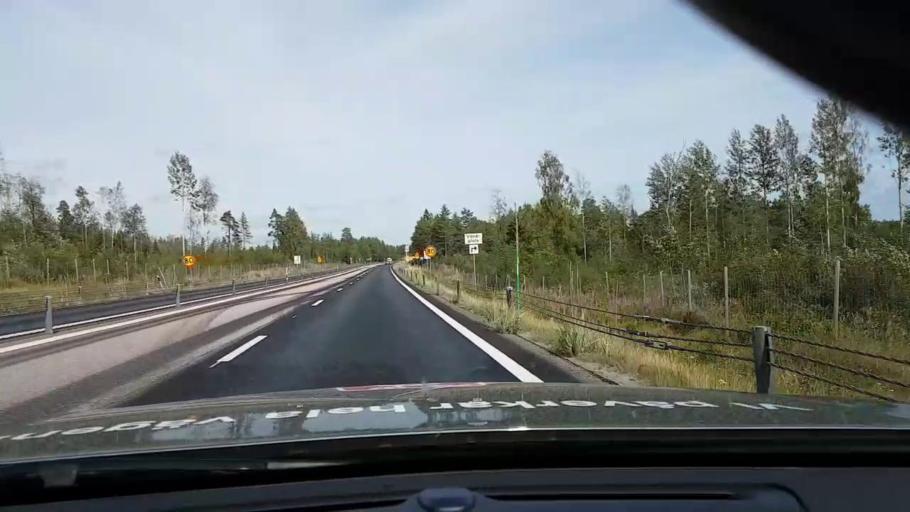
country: SE
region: Vaesternorrland
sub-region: OErnskoeldsviks Kommun
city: Husum
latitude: 63.4780
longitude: 19.2923
